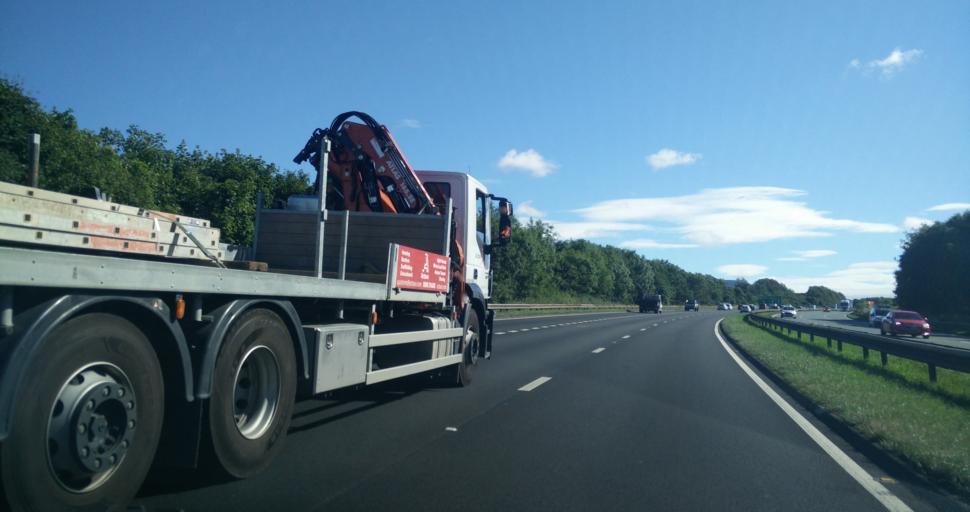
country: GB
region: England
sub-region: South Tyneside
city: The Boldons
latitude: 54.8989
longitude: -1.4554
